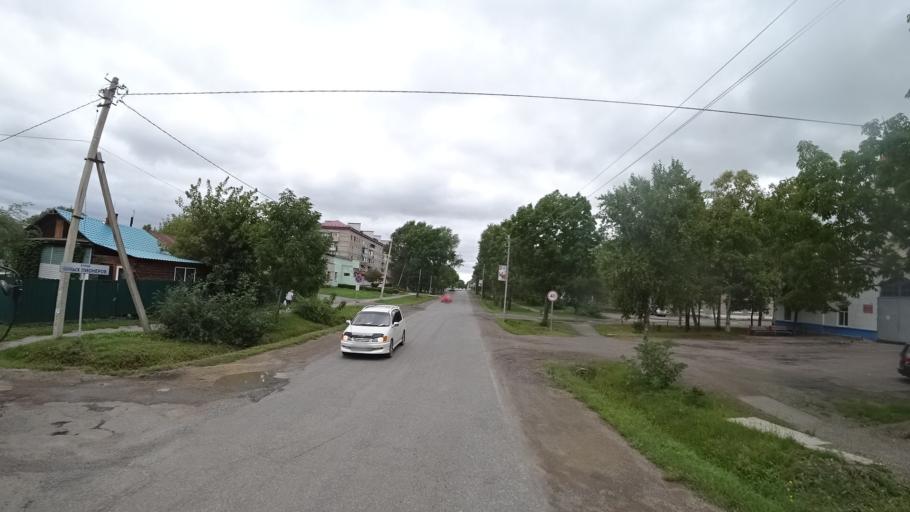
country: RU
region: Primorskiy
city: Chernigovka
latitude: 44.3417
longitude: 132.5779
